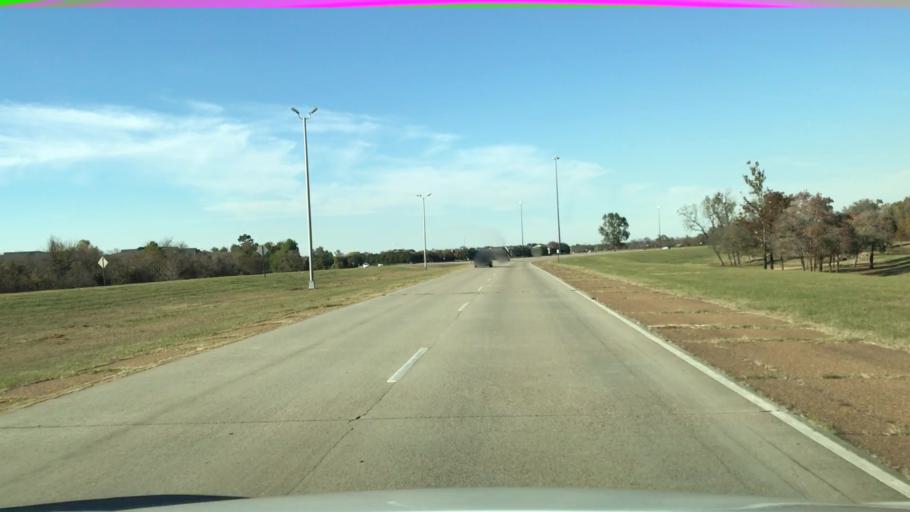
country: US
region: Louisiana
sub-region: Bossier Parish
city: Bossier City
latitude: 32.4646
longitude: -93.6844
